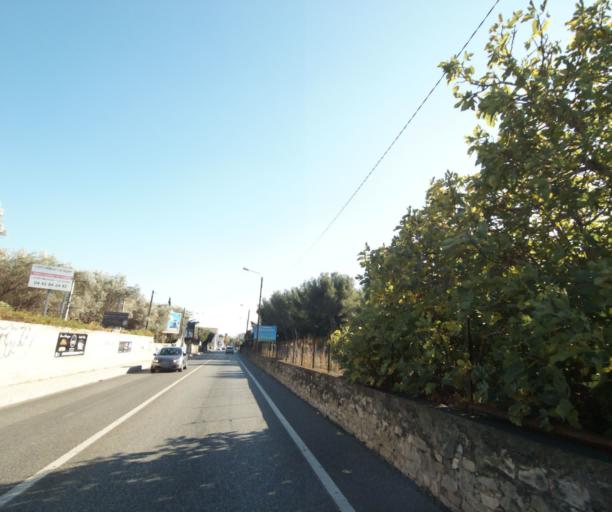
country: FR
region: Provence-Alpes-Cote d'Azur
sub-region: Departement des Bouches-du-Rhone
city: La Ciotat
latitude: 43.1869
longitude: 5.6065
